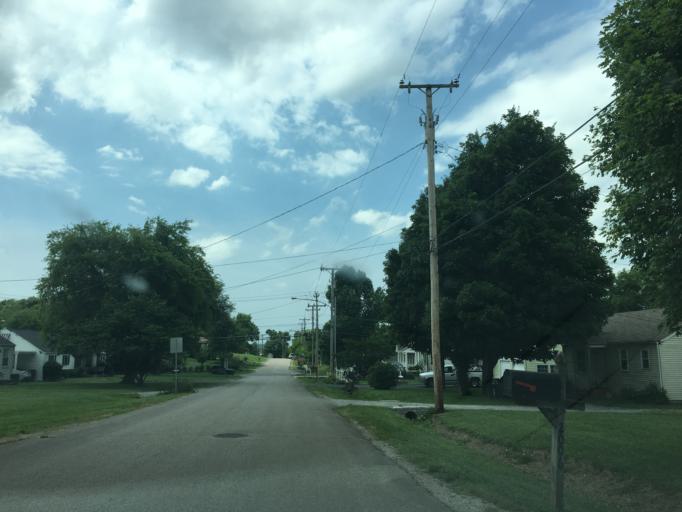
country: US
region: Tennessee
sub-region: Davidson County
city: Nashville
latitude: 36.1306
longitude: -86.7492
